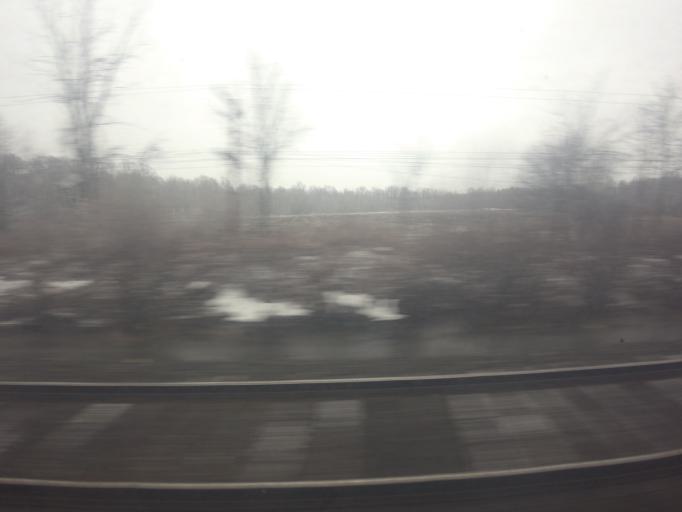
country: CA
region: Ontario
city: Brockville
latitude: 44.5711
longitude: -75.7570
